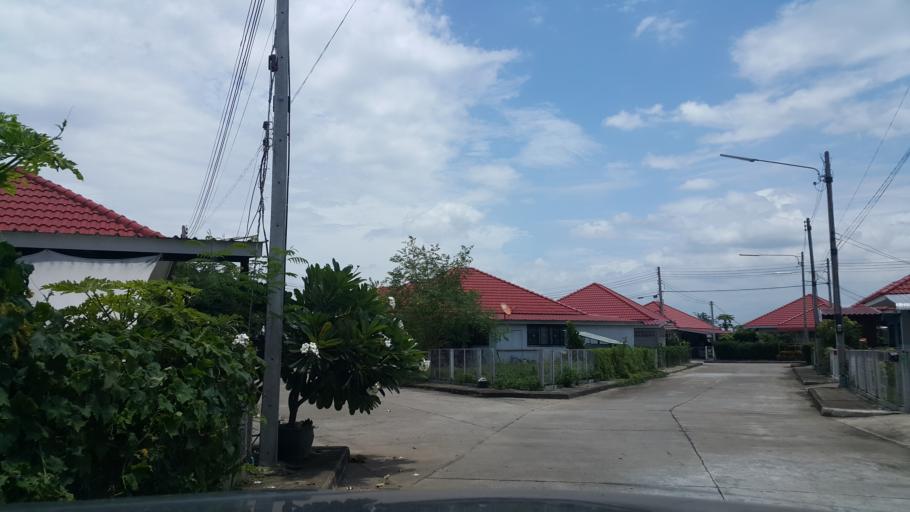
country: TH
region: Chiang Mai
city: Hang Dong
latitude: 18.7055
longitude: 98.9713
